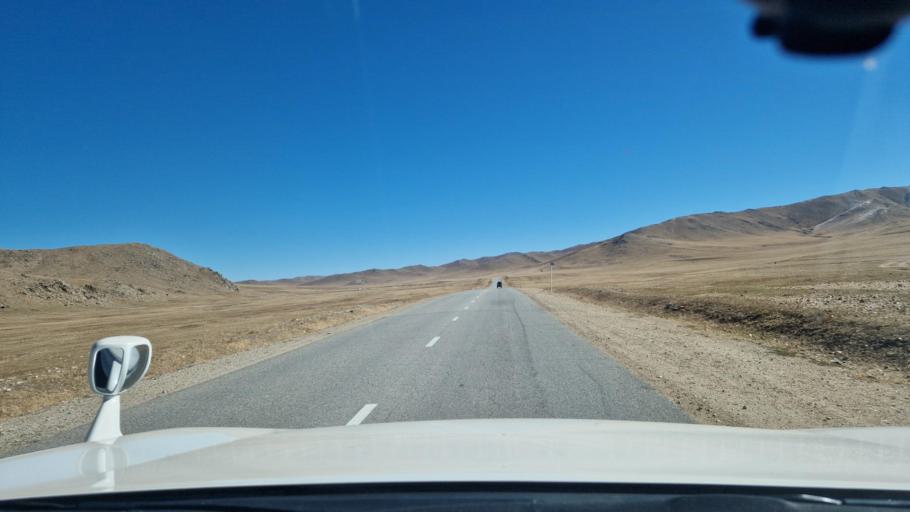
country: MN
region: Central Aimak
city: Bayandelger
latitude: 47.6938
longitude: 108.5160
